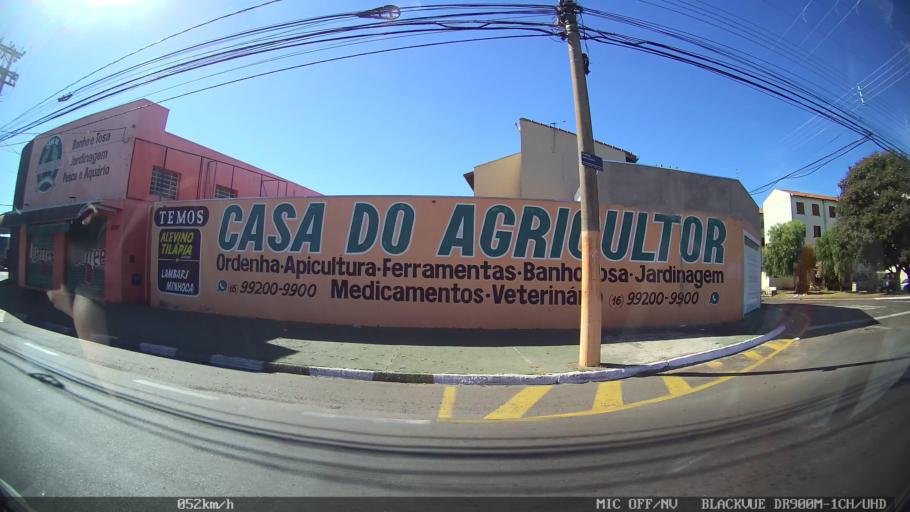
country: BR
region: Sao Paulo
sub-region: Franca
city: Franca
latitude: -20.5530
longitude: -47.3604
